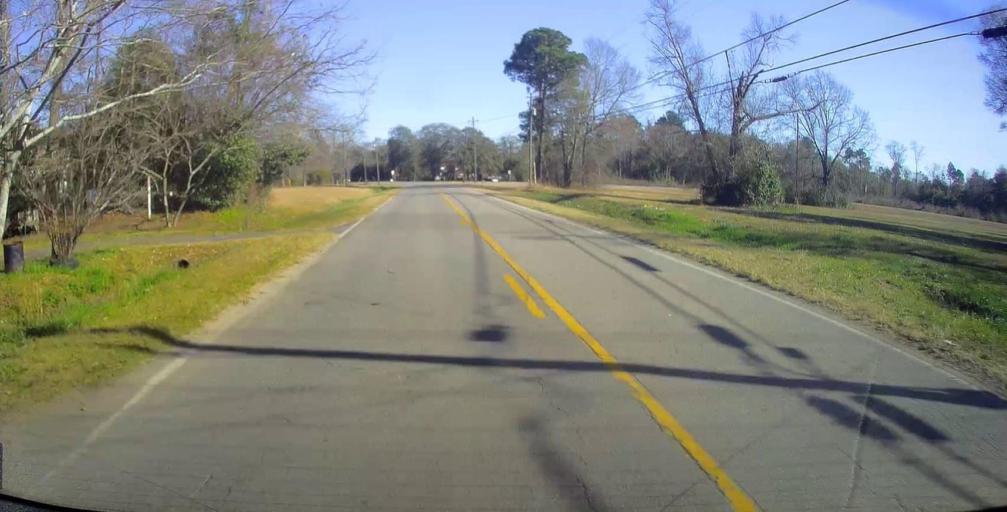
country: US
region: Georgia
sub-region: Taylor County
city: Butler
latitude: 32.5596
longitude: -84.2469
